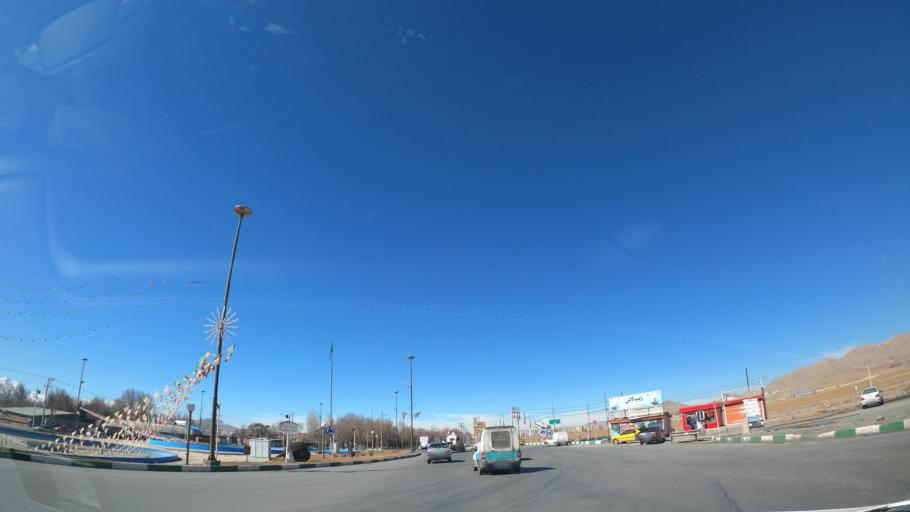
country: IR
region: Chahar Mahall va Bakhtiari
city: Shahrekord
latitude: 32.3076
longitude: 50.9025
